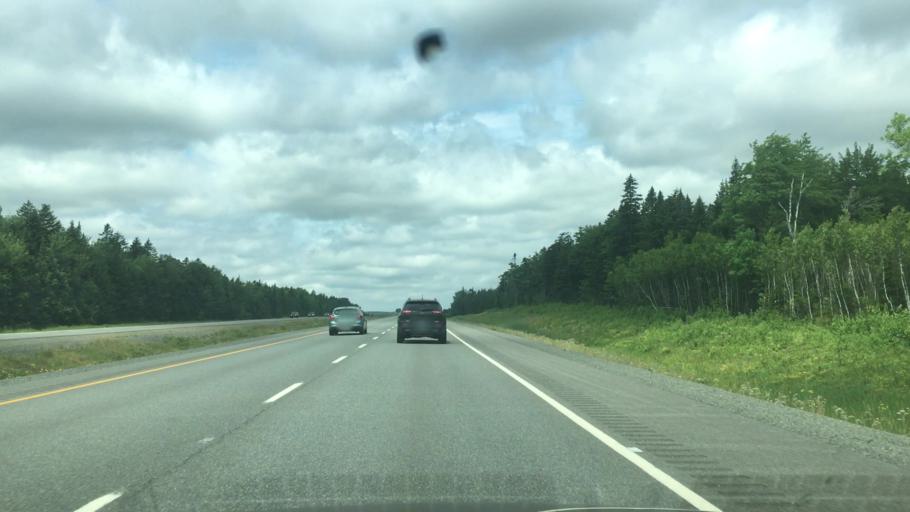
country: CA
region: Nova Scotia
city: Springhill
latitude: 45.7174
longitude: -64.0475
